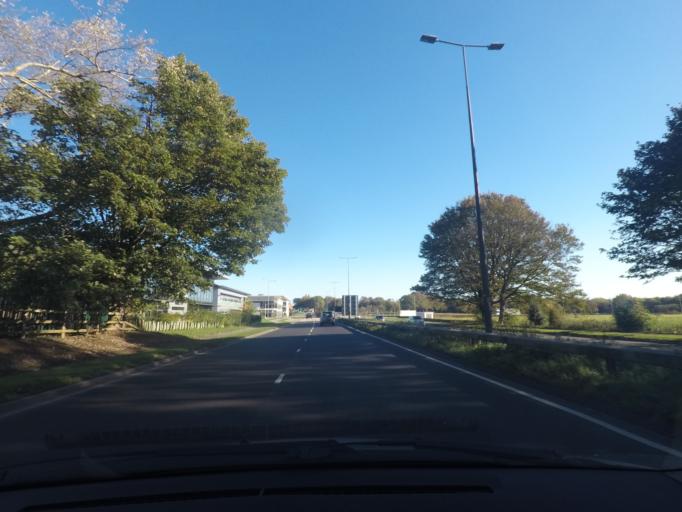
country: GB
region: England
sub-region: East Riding of Yorkshire
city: Hessle
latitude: 53.7228
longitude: -0.4620
